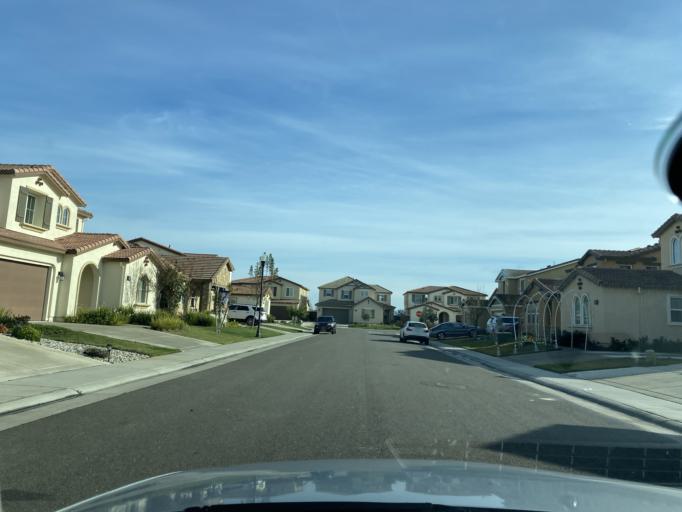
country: US
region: California
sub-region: Sacramento County
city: Elk Grove
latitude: 38.4035
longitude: -121.3975
